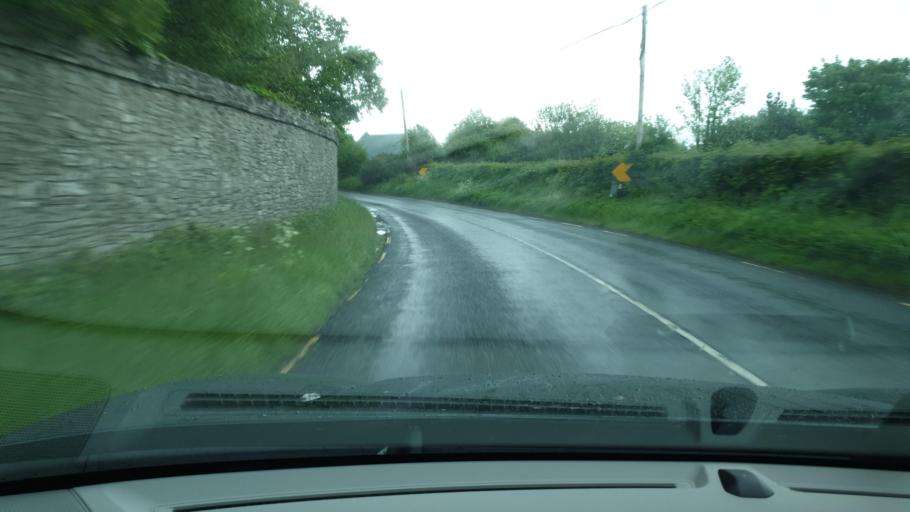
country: IE
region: Leinster
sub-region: Laois
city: Mountrath
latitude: 53.0614
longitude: -7.4147
